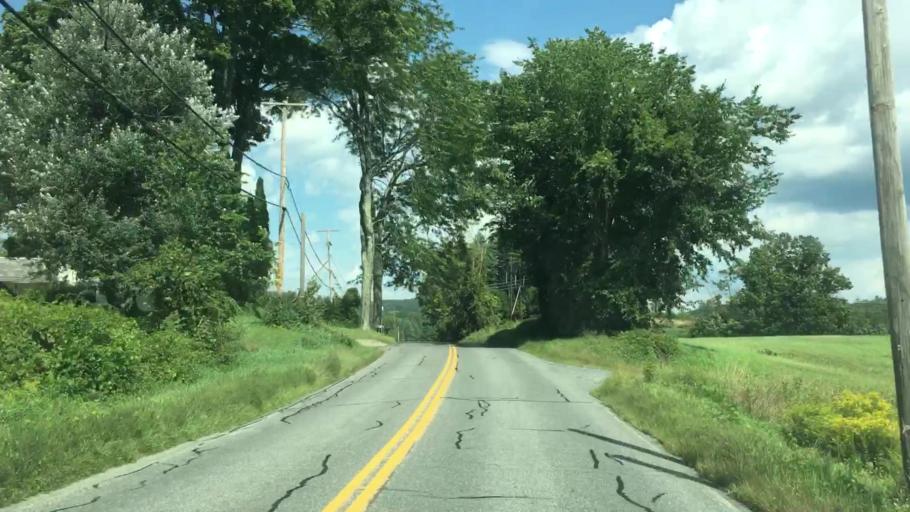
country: US
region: Vermont
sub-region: Windham County
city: West Brattleboro
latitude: 42.8025
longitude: -72.5948
